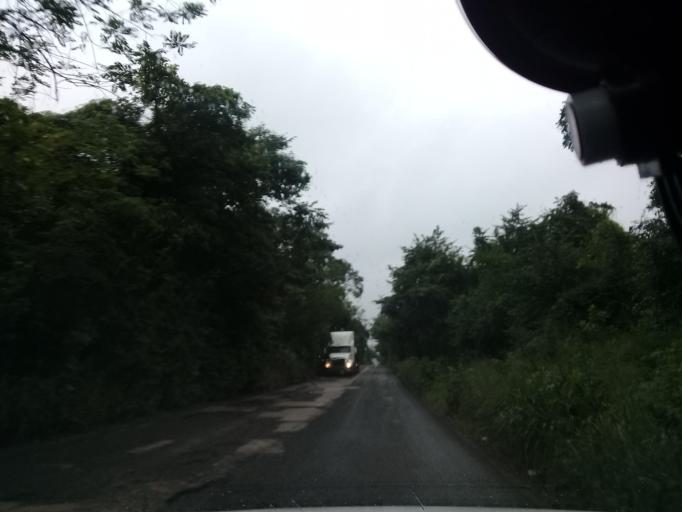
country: MX
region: Veracruz
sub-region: Chalma
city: San Pedro Coyutla
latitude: 21.2136
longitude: -98.3860
